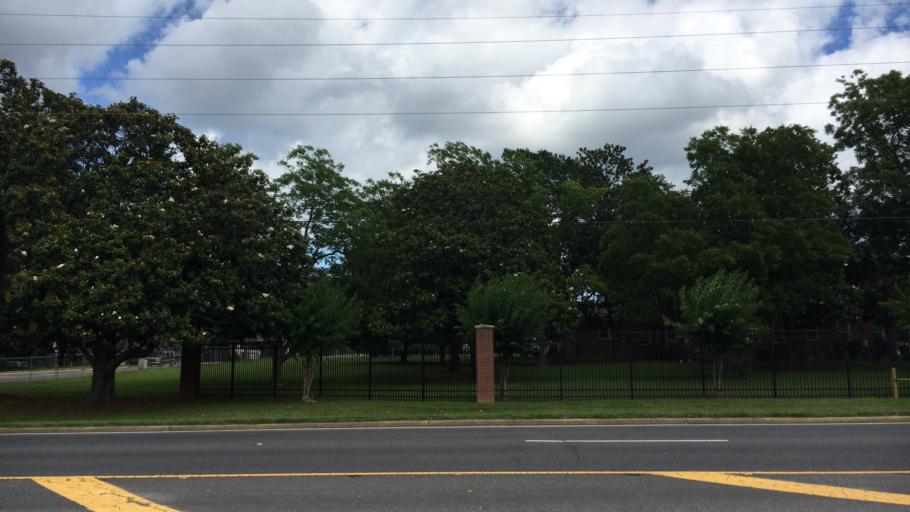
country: US
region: Louisiana
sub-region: Lincoln Parish
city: Ruston
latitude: 32.5194
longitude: -92.6388
